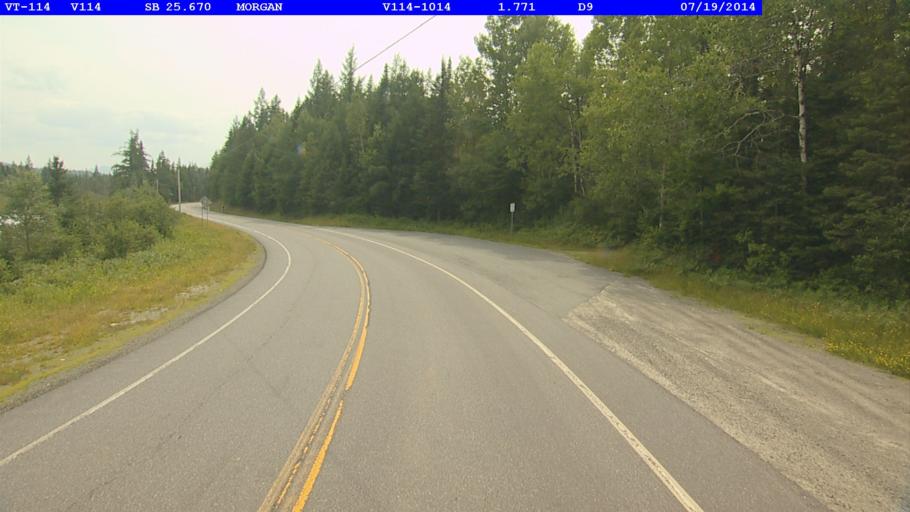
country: CA
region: Quebec
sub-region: Estrie
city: Coaticook
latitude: 44.8710
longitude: -71.9029
